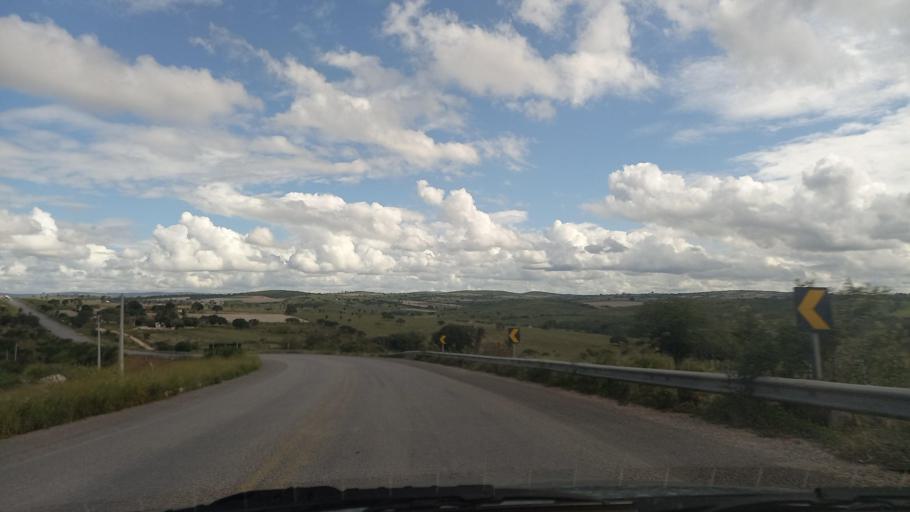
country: BR
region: Pernambuco
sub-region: Lajedo
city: Lajedo
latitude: -8.7270
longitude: -36.4314
